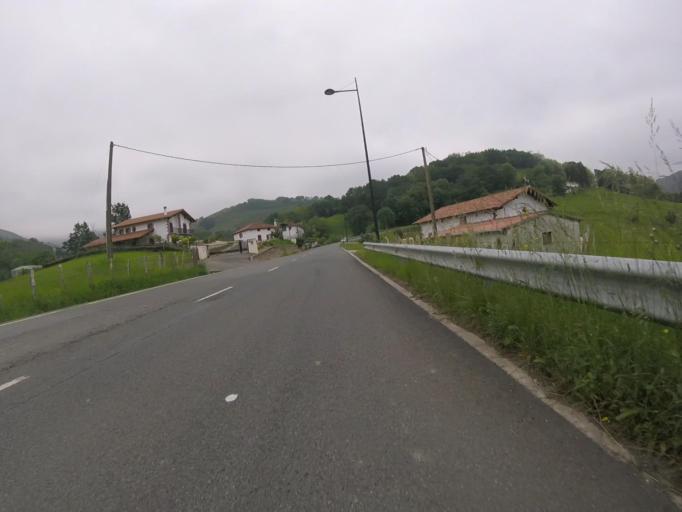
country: ES
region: Navarre
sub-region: Provincia de Navarra
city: Zugarramurdi
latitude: 43.2717
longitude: -1.4941
